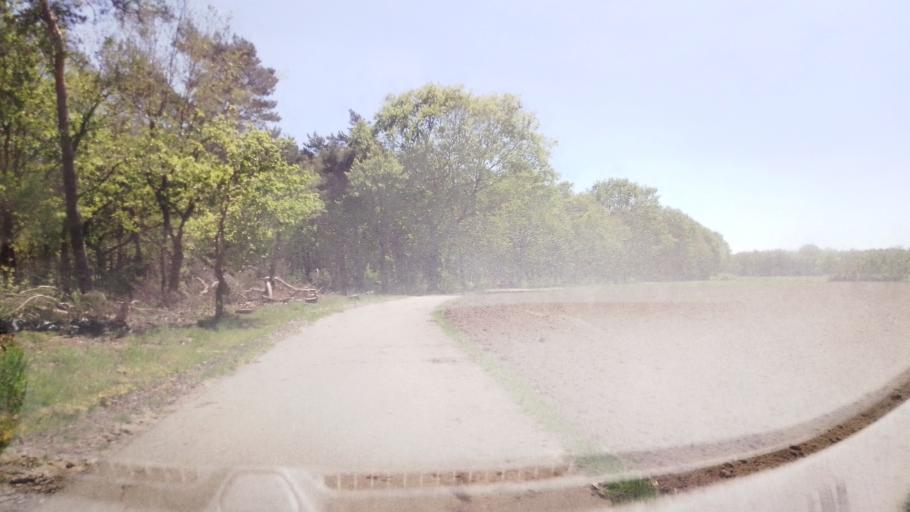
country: NL
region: Limburg
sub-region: Gemeente Venlo
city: Venlo
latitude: 51.4067
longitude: 6.1179
